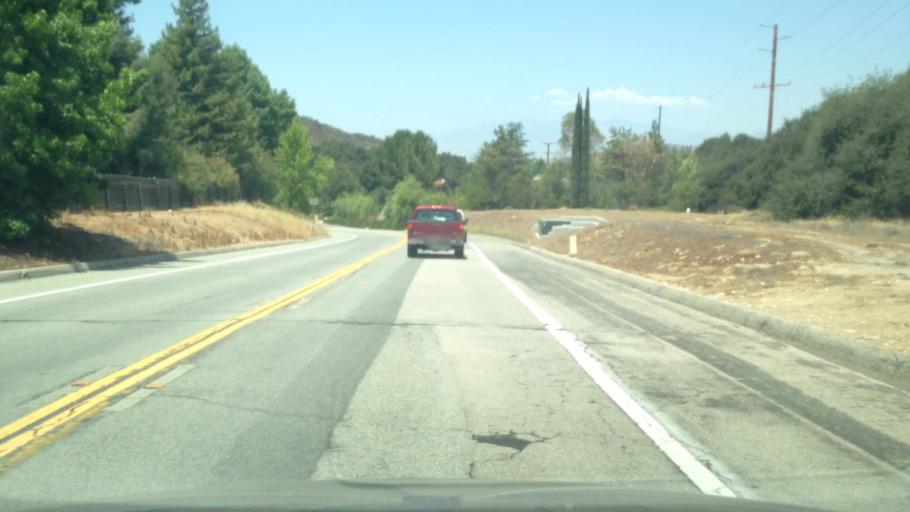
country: US
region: California
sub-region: Riverside County
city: Cherry Valley
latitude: 34.0104
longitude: -116.9896
